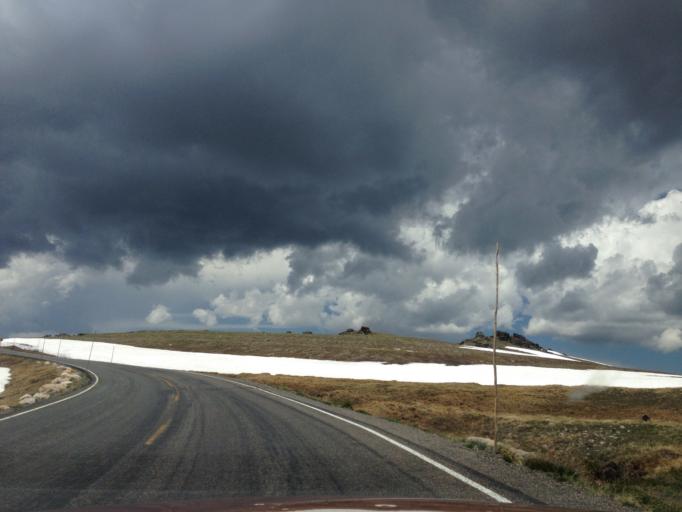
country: US
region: Colorado
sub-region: Larimer County
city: Estes Park
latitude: 40.4100
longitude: -105.7186
